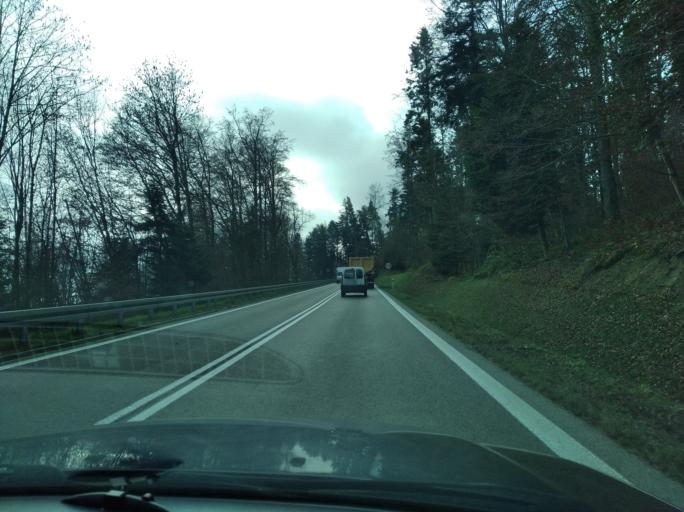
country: PL
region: Subcarpathian Voivodeship
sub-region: Powiat brzozowski
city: Jablonica Polska
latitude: 49.7284
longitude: 21.9072
